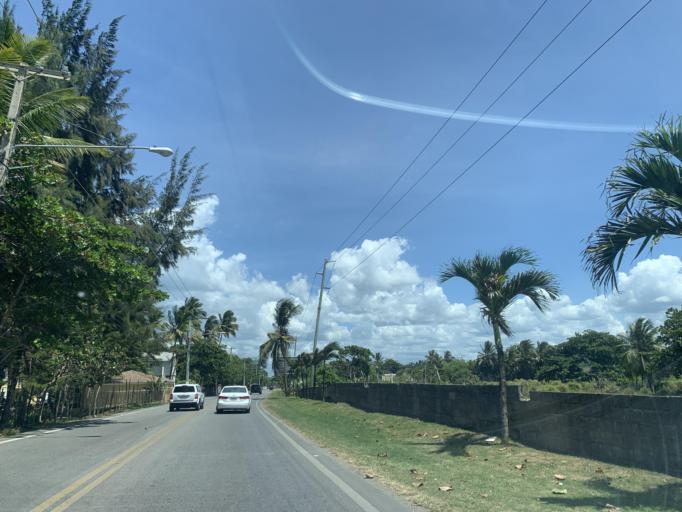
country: DO
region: Puerto Plata
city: Cabarete
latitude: 19.7456
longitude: -70.3951
